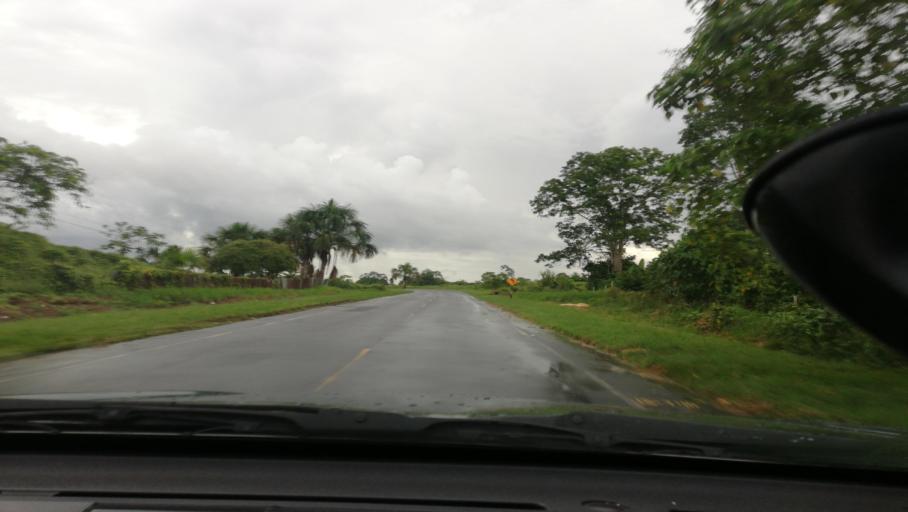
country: PE
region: Loreto
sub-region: Provincia de Maynas
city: San Juan
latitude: -3.9178
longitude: -73.3679
